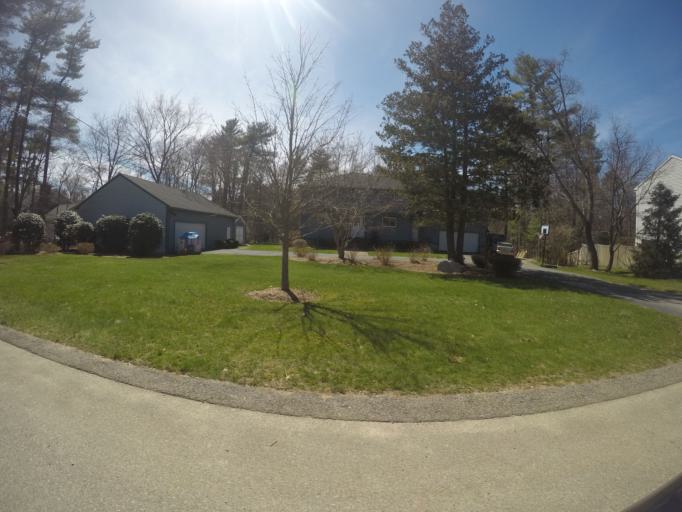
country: US
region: Massachusetts
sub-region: Bristol County
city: Easton
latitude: 42.0300
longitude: -71.0928
